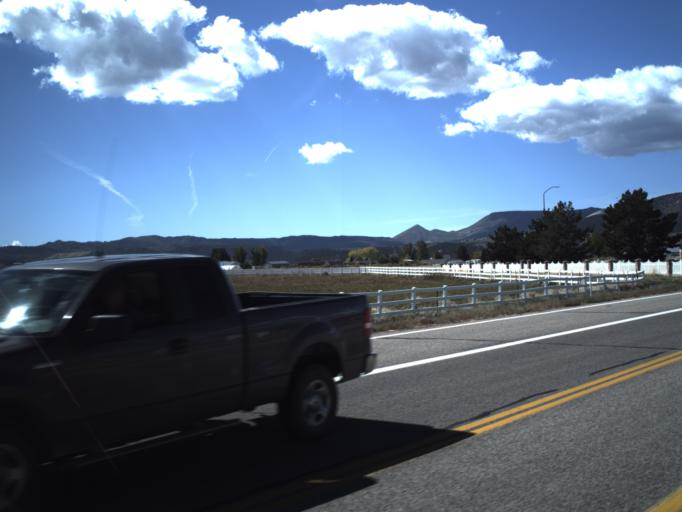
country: US
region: Utah
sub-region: Washington County
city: Enterprise
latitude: 37.5740
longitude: -113.7030
